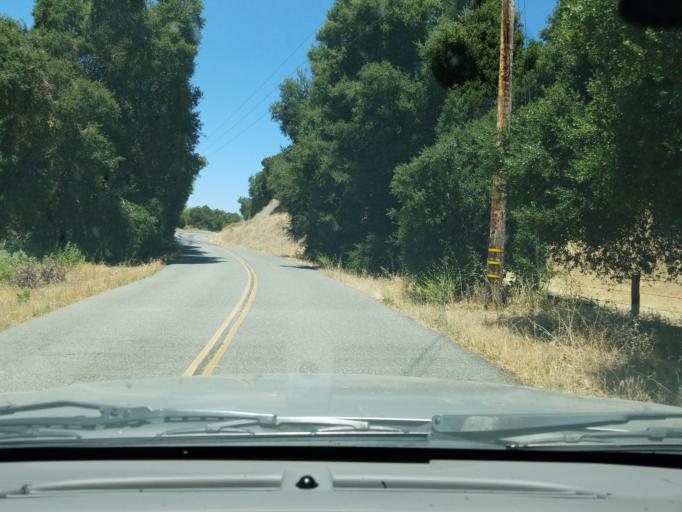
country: US
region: California
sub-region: Monterey County
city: Carmel Valley Village
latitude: 36.4399
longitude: -121.6377
